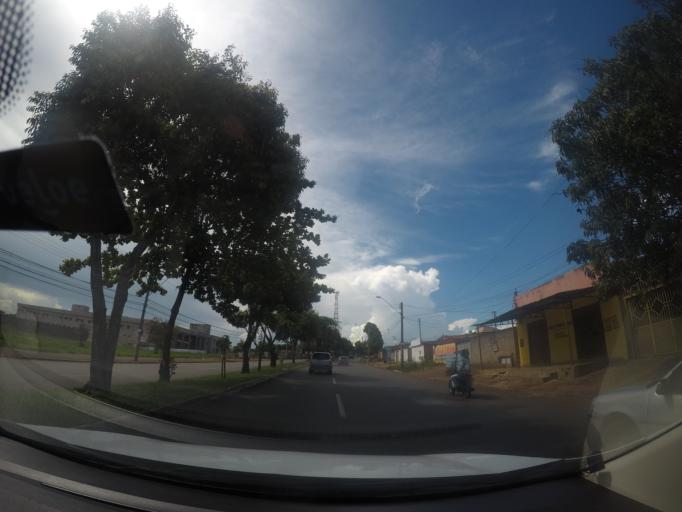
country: BR
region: Goias
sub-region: Trindade
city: Trindade
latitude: -16.6645
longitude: -49.3870
